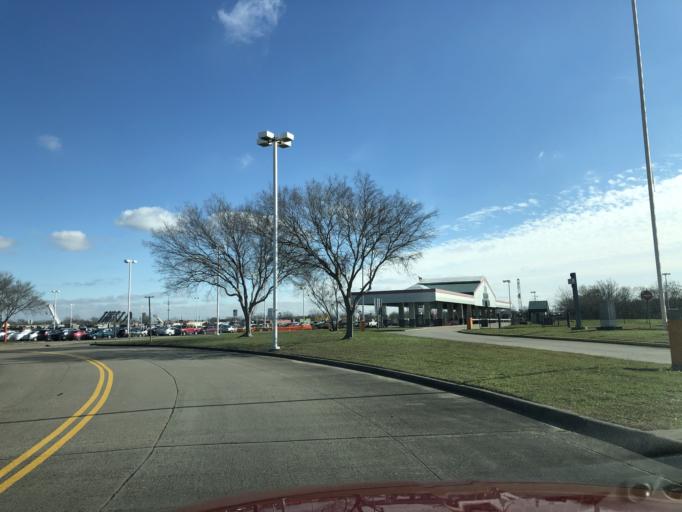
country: US
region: Texas
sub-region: Harris County
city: South Houston
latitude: 29.6635
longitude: -95.2559
